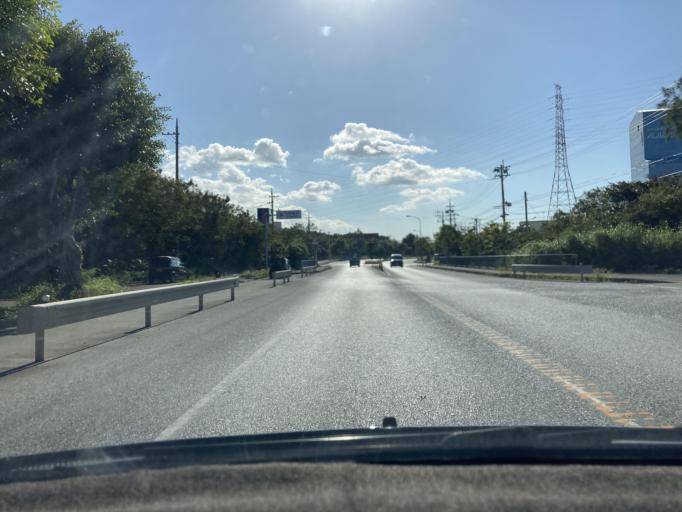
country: JP
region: Okinawa
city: Ishikawa
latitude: 26.4366
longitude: 127.8417
